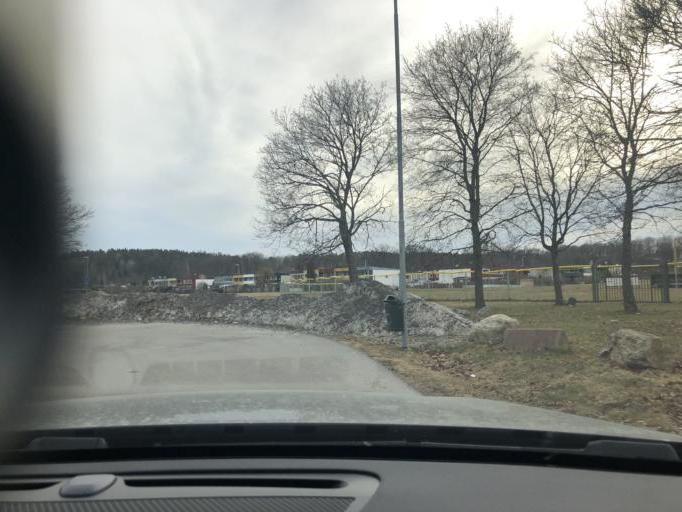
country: SE
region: Stockholm
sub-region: Botkyrka Kommun
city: Fittja
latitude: 59.2383
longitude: 17.8641
